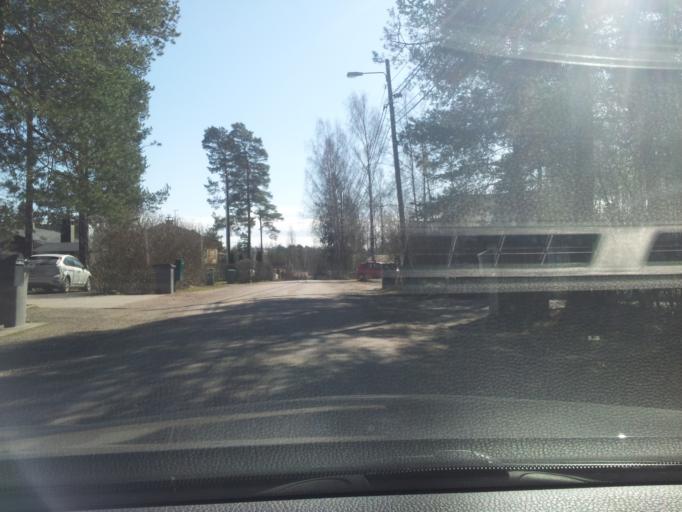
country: FI
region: Uusimaa
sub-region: Helsinki
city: Kauniainen
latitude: 60.1705
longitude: 24.7208
